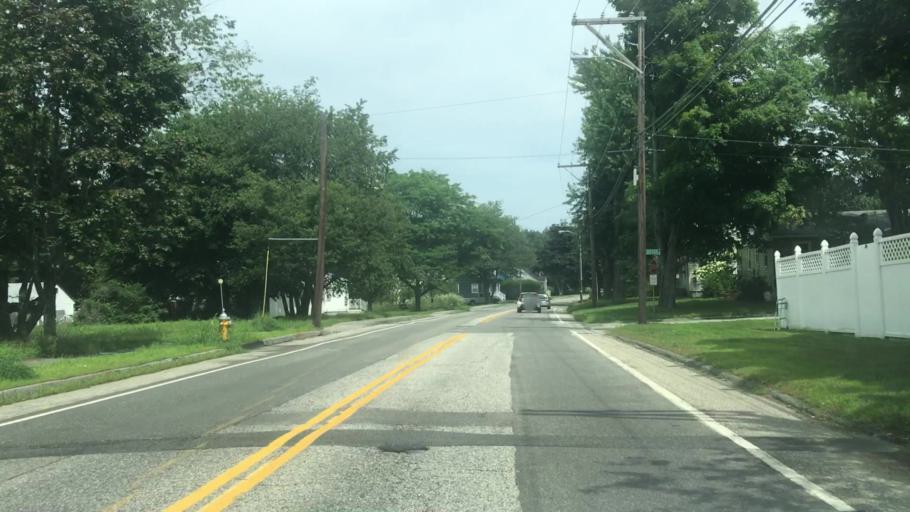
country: US
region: Maine
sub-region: Cumberland County
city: South Portland
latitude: 43.6161
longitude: -70.2766
